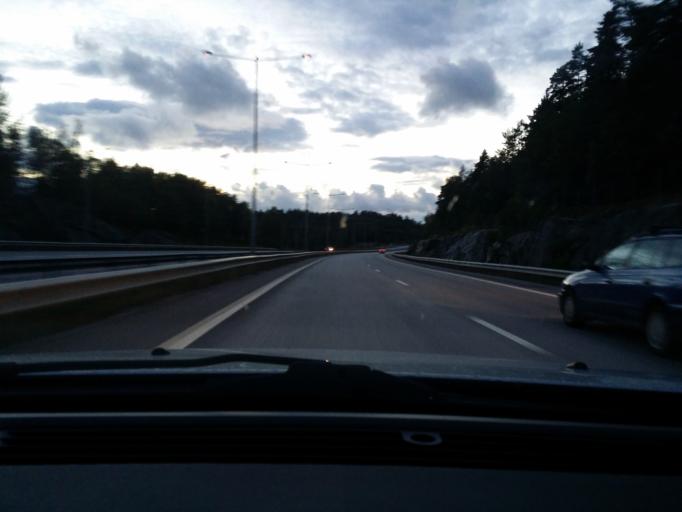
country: SE
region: Stockholm
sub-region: Upplands-Bro Kommun
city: Bro
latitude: 59.5279
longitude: 17.6381
